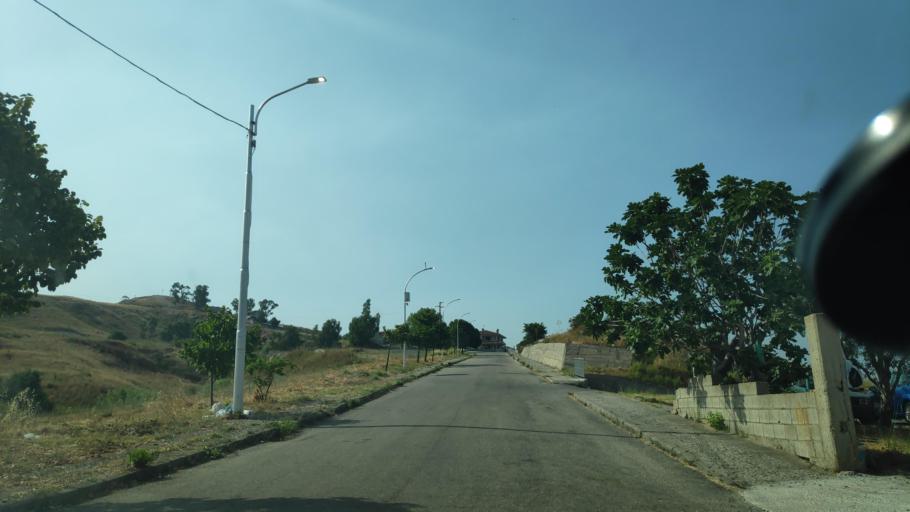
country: IT
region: Calabria
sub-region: Provincia di Catanzaro
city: Santa Caterina dello Ionio Marina
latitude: 38.5298
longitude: 16.5687
